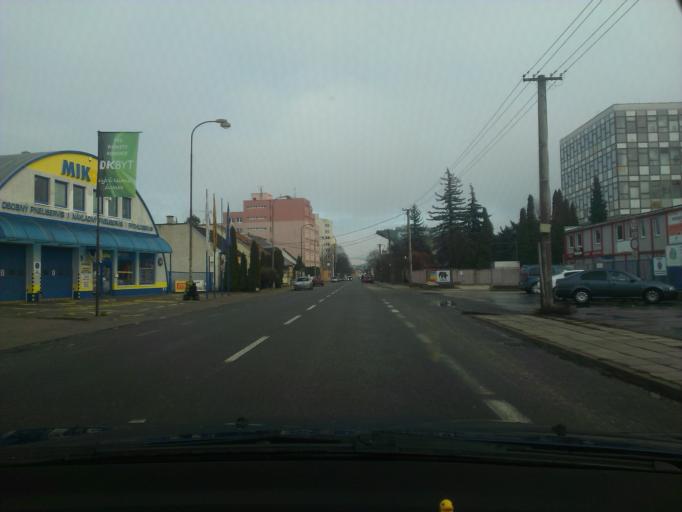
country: SK
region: Trnavsky
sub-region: Okres Trnava
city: Piestany
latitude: 48.5921
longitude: 17.8134
